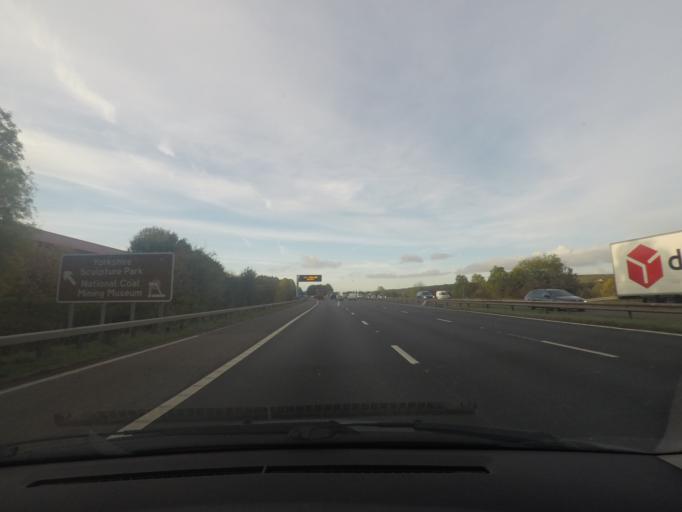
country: GB
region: England
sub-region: Barnsley
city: Darton
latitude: 53.5902
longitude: -1.5375
